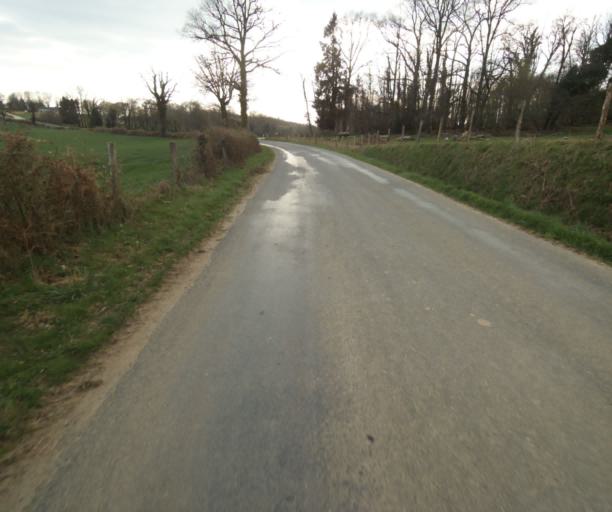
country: FR
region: Limousin
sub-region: Departement de la Correze
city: Saint-Clement
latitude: 45.3628
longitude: 1.6424
